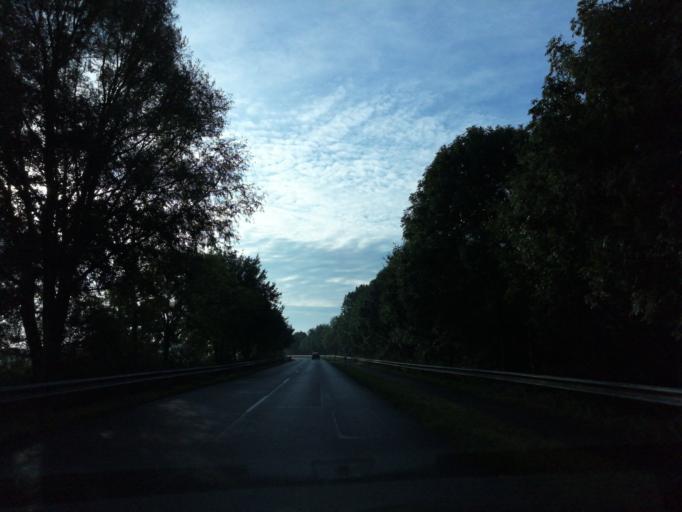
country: DE
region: Lower Saxony
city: Sillenstede
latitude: 53.6260
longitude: 8.0149
